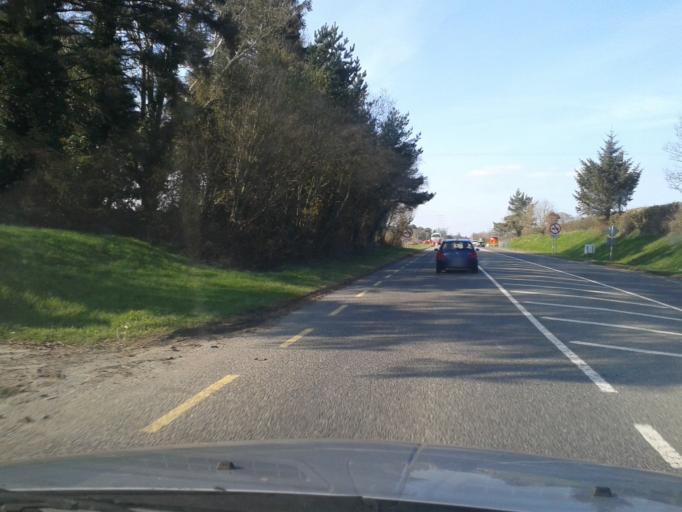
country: IE
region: Leinster
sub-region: Wicklow
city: Rathnew
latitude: 52.9579
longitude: -6.0946
